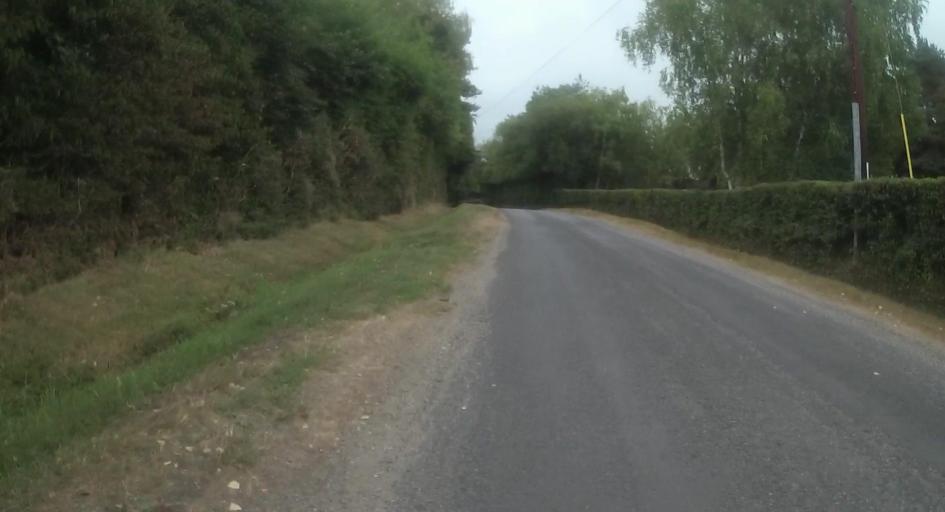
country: GB
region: England
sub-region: Dorset
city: Wool
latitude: 50.7100
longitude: -2.2009
